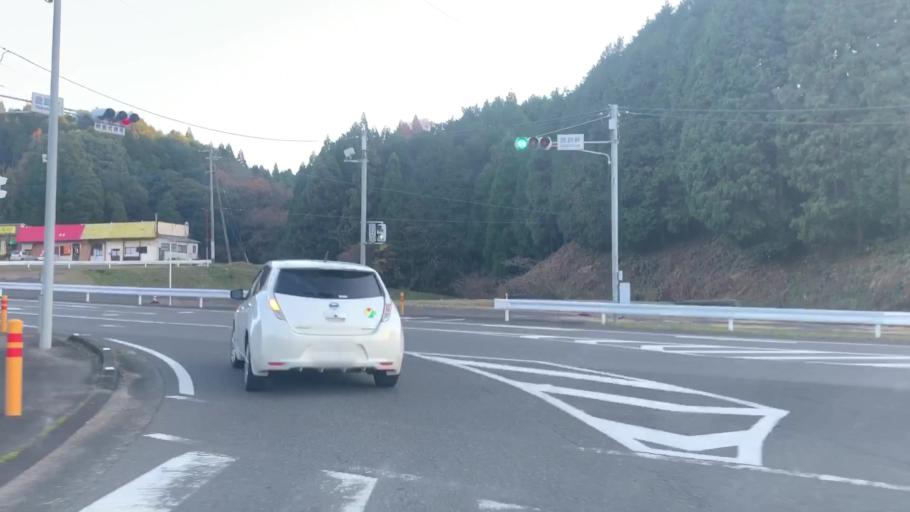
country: JP
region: Saga Prefecture
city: Imaricho-ko
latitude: 33.2638
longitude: 129.9659
